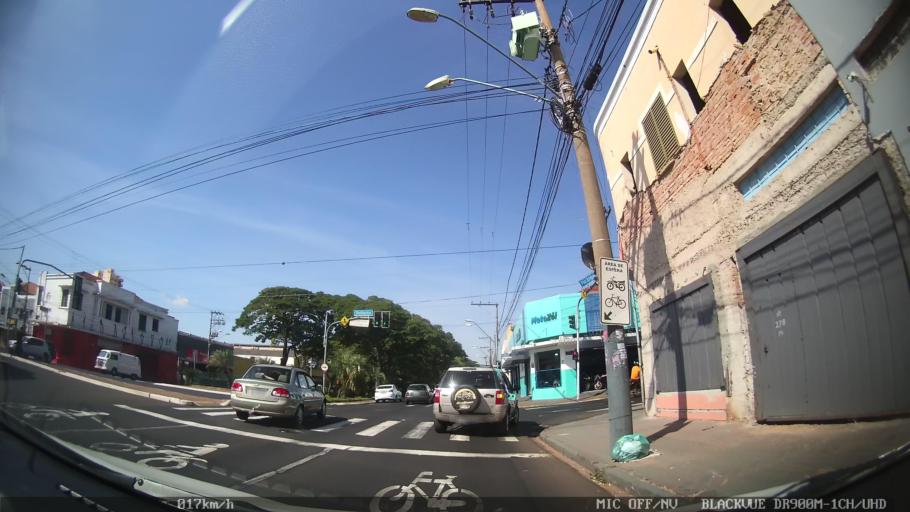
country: BR
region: Sao Paulo
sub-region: Ribeirao Preto
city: Ribeirao Preto
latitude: -21.1708
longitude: -47.8091
